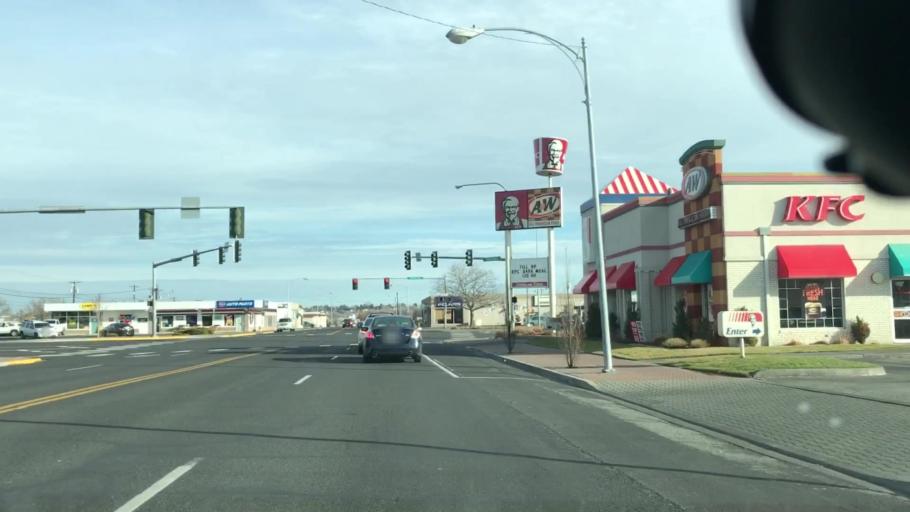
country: US
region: Washington
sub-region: Grant County
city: Moses Lake
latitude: 47.1321
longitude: -119.2741
